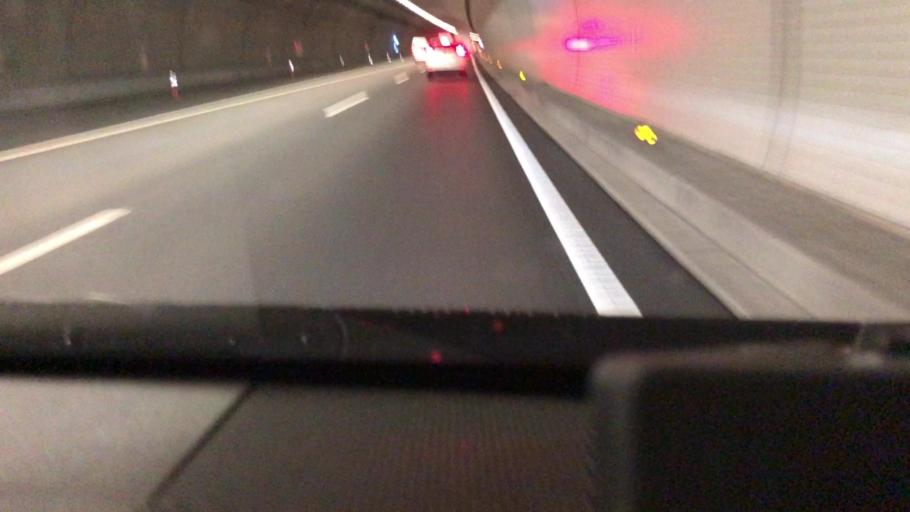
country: JP
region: Shizuoka
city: Shimada
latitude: 34.8788
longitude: 138.1874
